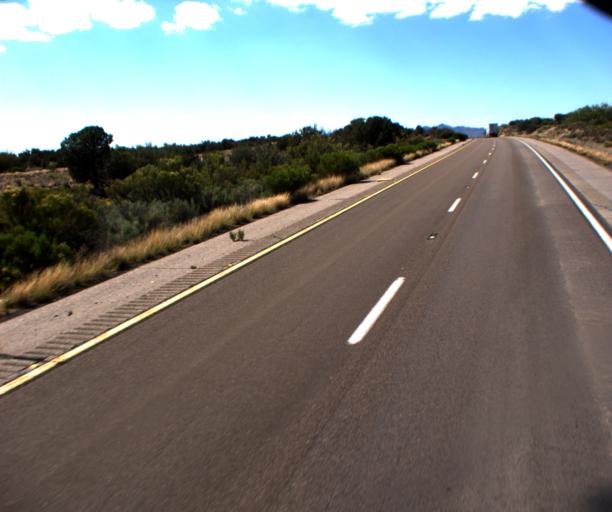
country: US
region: Arizona
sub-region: Mohave County
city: New Kingman-Butler
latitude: 35.1343
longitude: -113.6690
